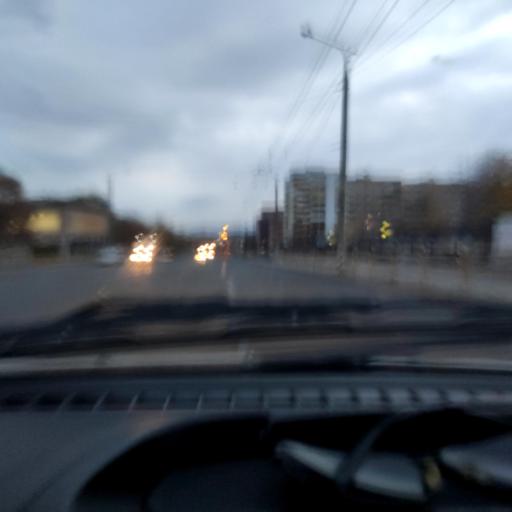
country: RU
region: Samara
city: Zhigulevsk
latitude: 53.4753
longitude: 49.4644
